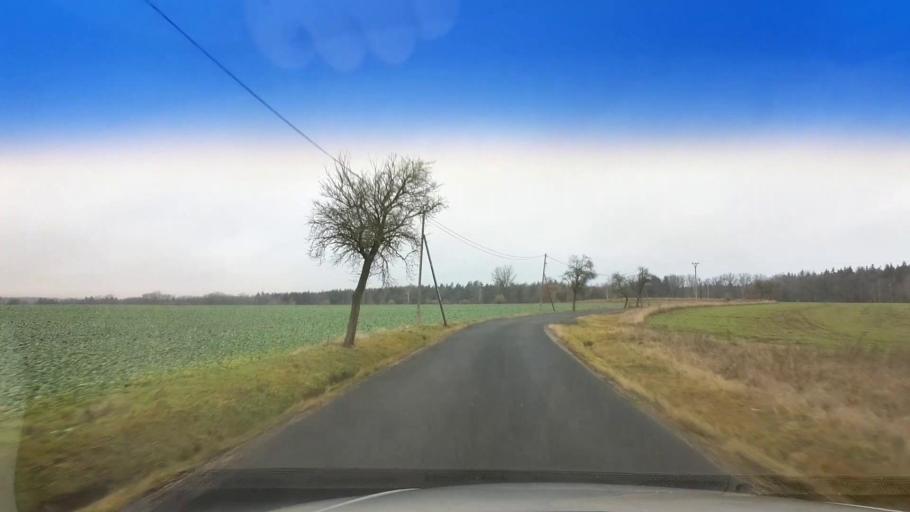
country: CZ
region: Karlovarsky
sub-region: Okres Cheb
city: Cheb
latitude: 50.0395
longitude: 12.3670
